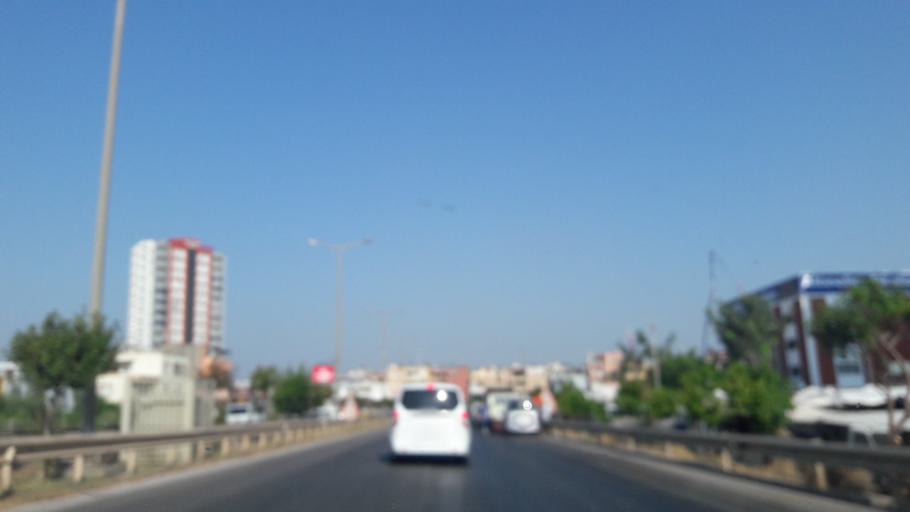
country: TR
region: Adana
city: Yuregir
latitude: 37.0239
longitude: 35.4006
